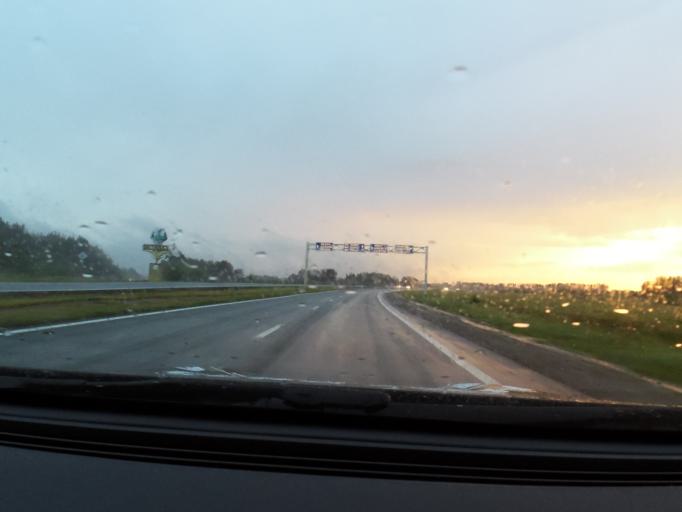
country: RU
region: Tatarstan
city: Yelabuga
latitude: 55.7815
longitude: 52.1819
